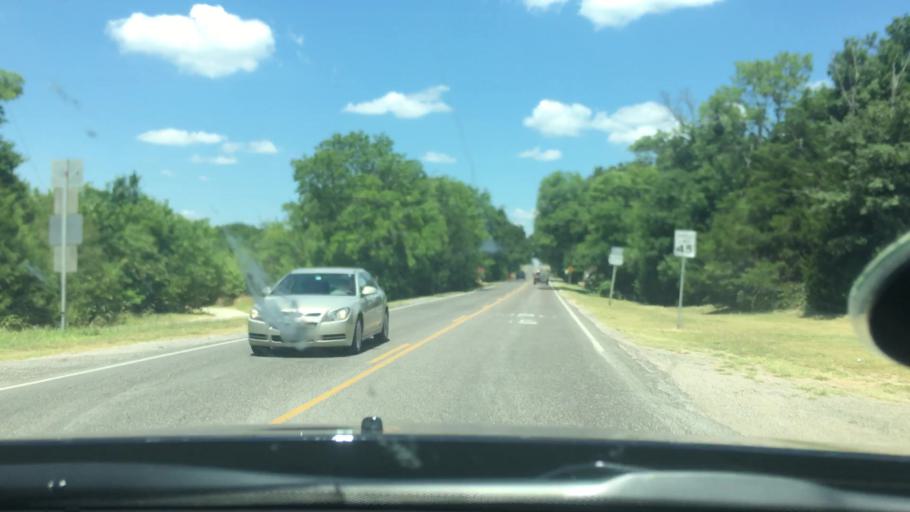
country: US
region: Oklahoma
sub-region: Murray County
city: Sulphur
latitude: 34.4917
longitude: -96.9665
